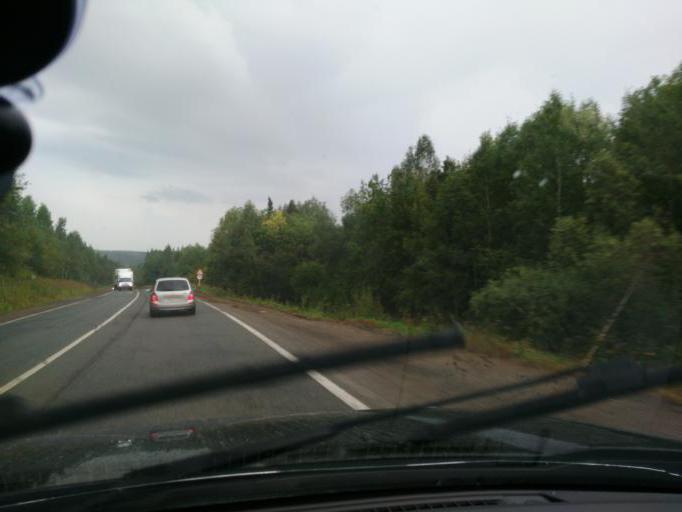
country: RU
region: Perm
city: Barda
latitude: 56.8911
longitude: 55.7682
